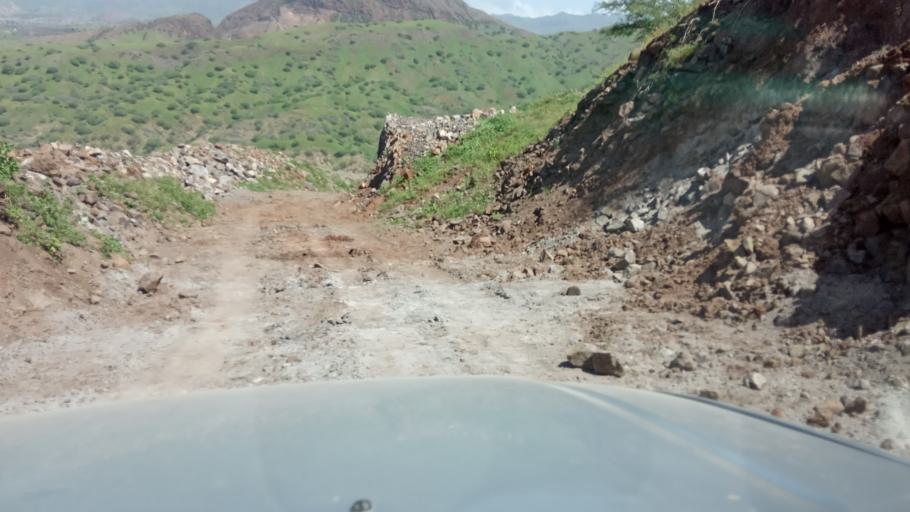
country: CV
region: Santa Catarina
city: Assomada
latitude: 15.1101
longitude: -23.7292
